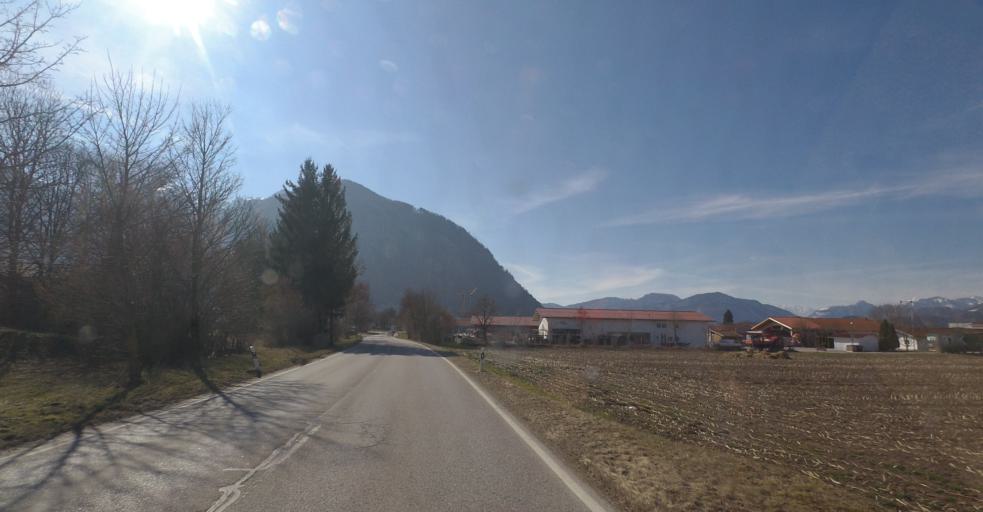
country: DE
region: Bavaria
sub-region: Upper Bavaria
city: Staudach-Egerndach
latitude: 47.7817
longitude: 12.4747
